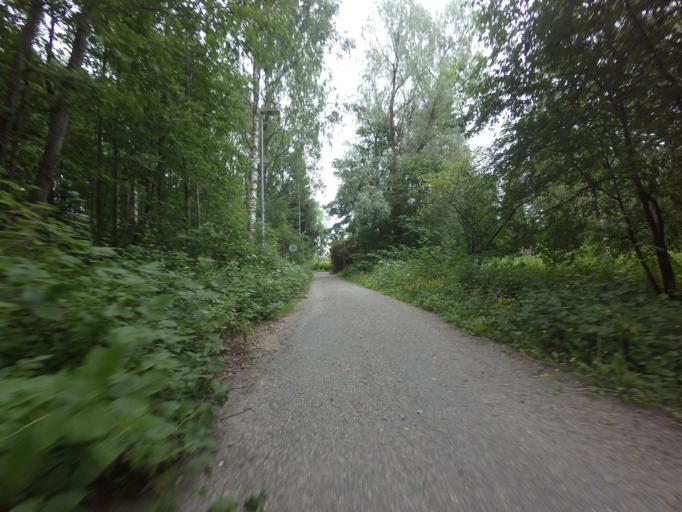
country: FI
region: Uusimaa
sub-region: Helsinki
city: Kauniainen
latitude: 60.1896
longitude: 24.7296
